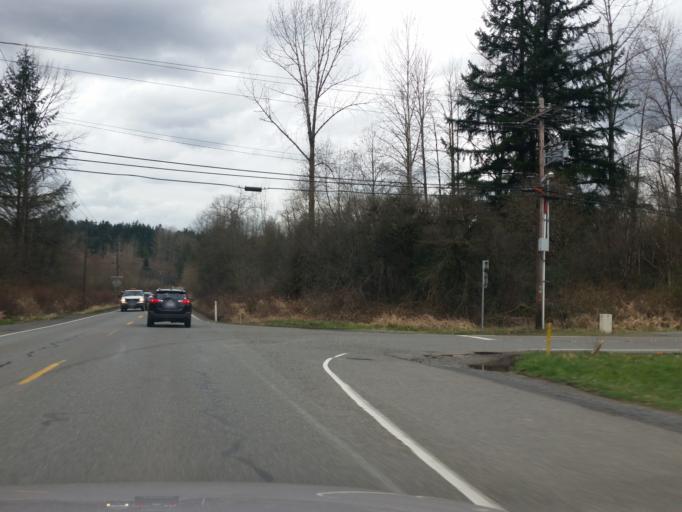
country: US
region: Washington
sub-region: Snohomish County
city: North Creek
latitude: 47.8050
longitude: -122.1522
